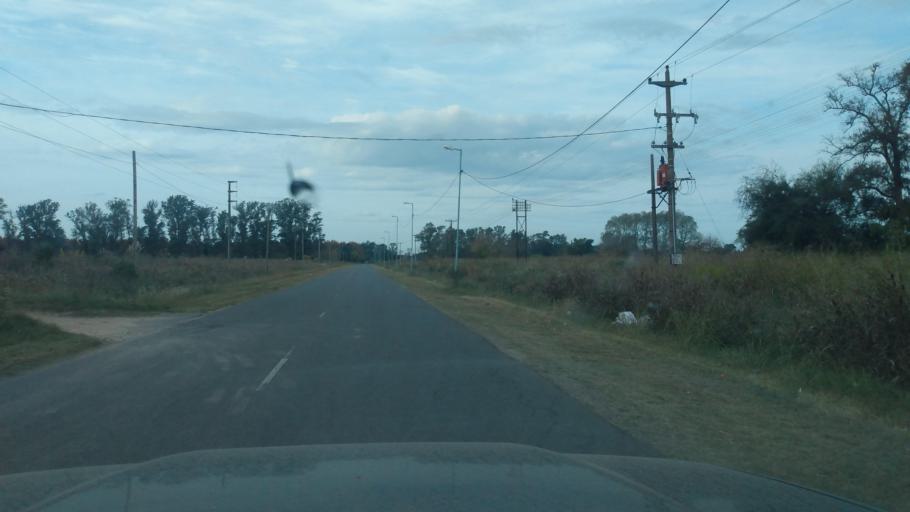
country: AR
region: Buenos Aires
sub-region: Partido de Lujan
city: Lujan
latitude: -34.5973
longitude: -59.1642
